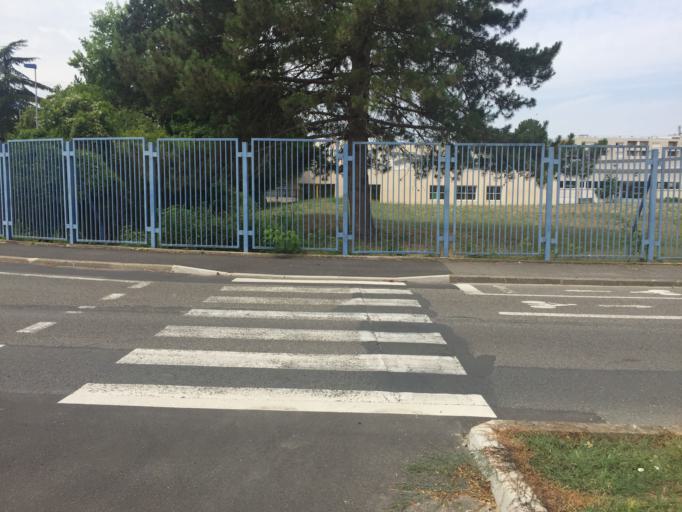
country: FR
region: Ile-de-France
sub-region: Departement de Seine-et-Marne
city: Nanteuil-les-Meaux
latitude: 48.9474
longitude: 2.9105
